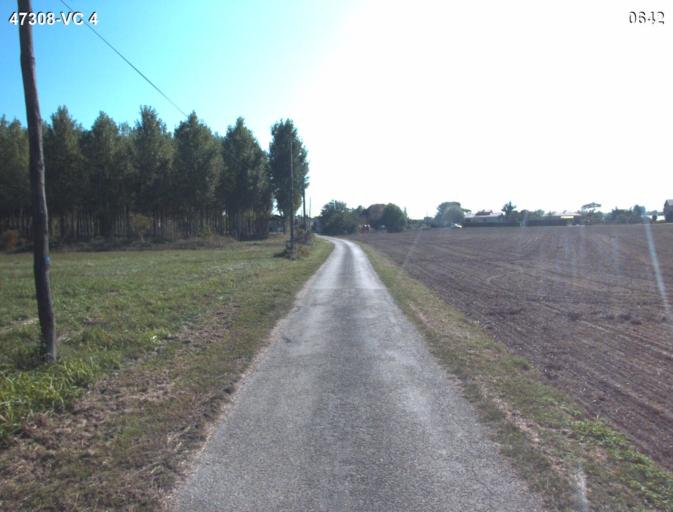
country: FR
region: Aquitaine
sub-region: Departement du Lot-et-Garonne
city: Buzet-sur-Baise
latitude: 44.2606
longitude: 0.3318
